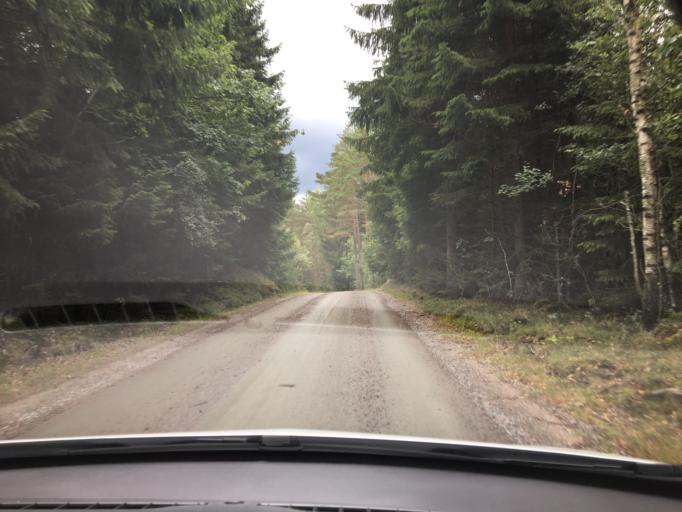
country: SE
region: Vaestra Goetaland
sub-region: Ale Kommun
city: Nodinge-Nol
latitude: 57.8783
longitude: 12.0823
